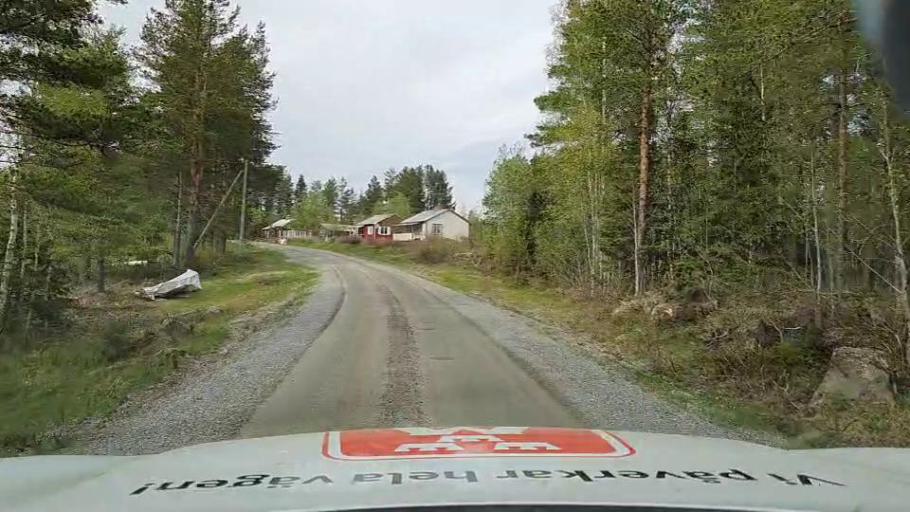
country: SE
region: Jaemtland
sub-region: OEstersunds Kommun
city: Brunflo
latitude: 62.5889
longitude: 14.9101
